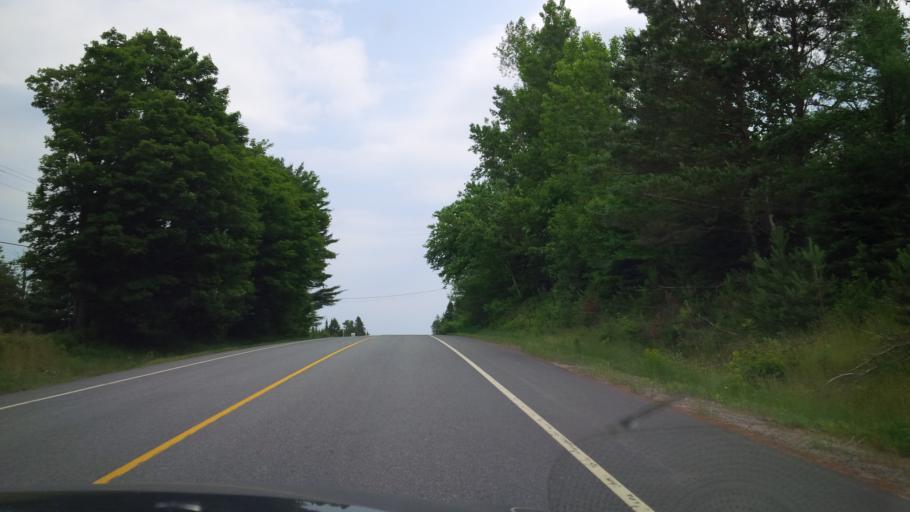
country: CA
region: Ontario
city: Huntsville
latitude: 45.5371
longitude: -79.2878
